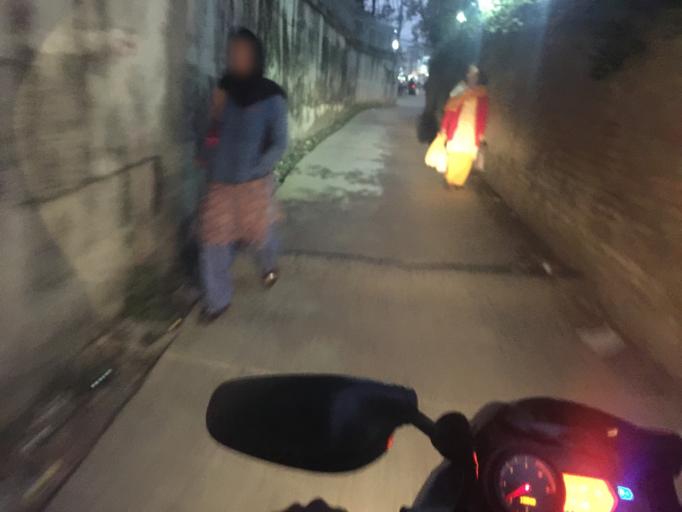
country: NP
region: Central Region
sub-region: Bagmati Zone
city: Patan
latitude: 27.6771
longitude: 85.3071
